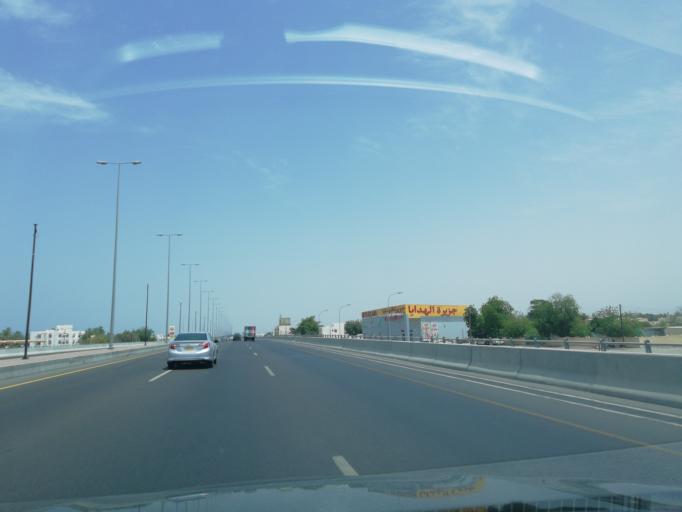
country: OM
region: Muhafazat Masqat
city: As Sib al Jadidah
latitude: 23.6721
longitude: 58.1445
